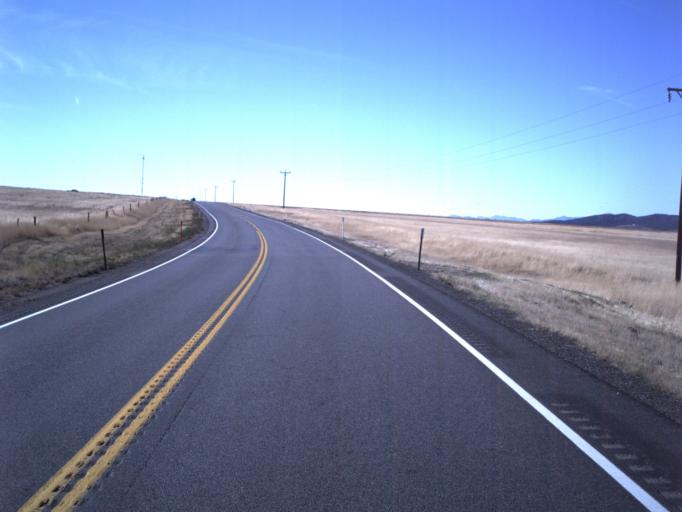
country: US
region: Utah
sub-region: Juab County
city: Nephi
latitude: 39.6666
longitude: -111.8516
